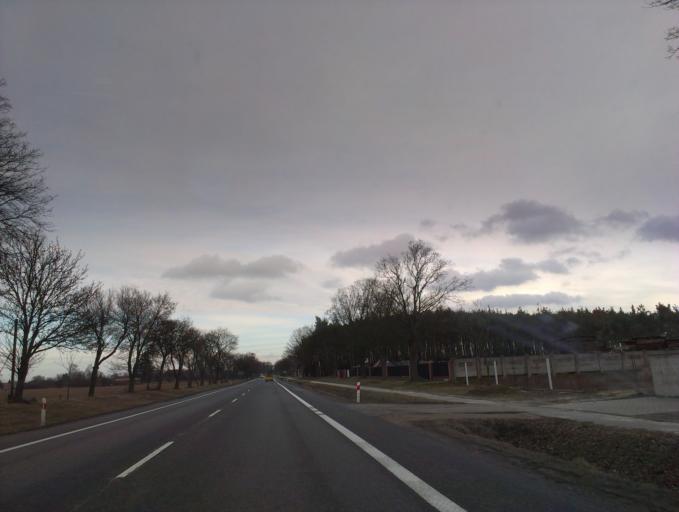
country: PL
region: Masovian Voivodeship
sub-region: Powiat sierpecki
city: Sierpc
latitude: 52.8679
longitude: 19.6517
